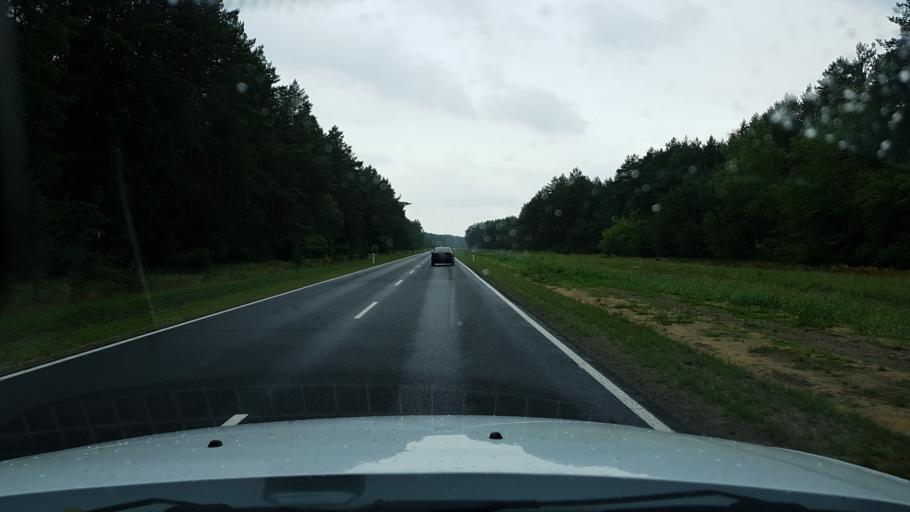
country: PL
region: West Pomeranian Voivodeship
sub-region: Powiat stargardzki
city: Kobylanka
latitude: 53.4312
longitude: 14.8407
